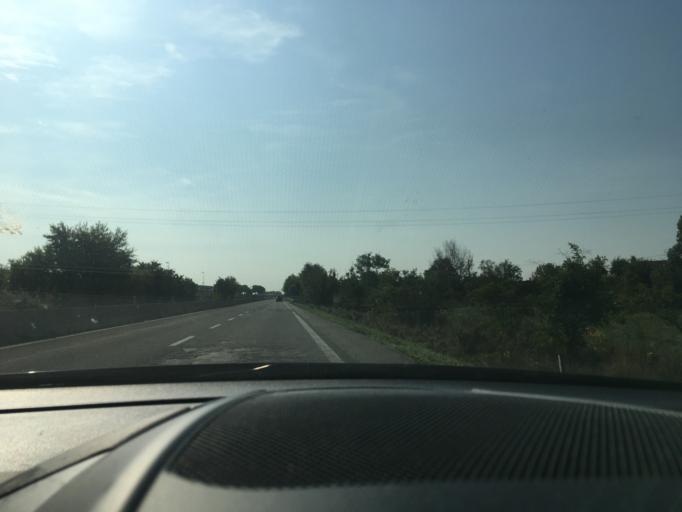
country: IT
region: Emilia-Romagna
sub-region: Provincia di Rimini
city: Bellaria-Igea Marina
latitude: 44.1320
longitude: 12.4656
